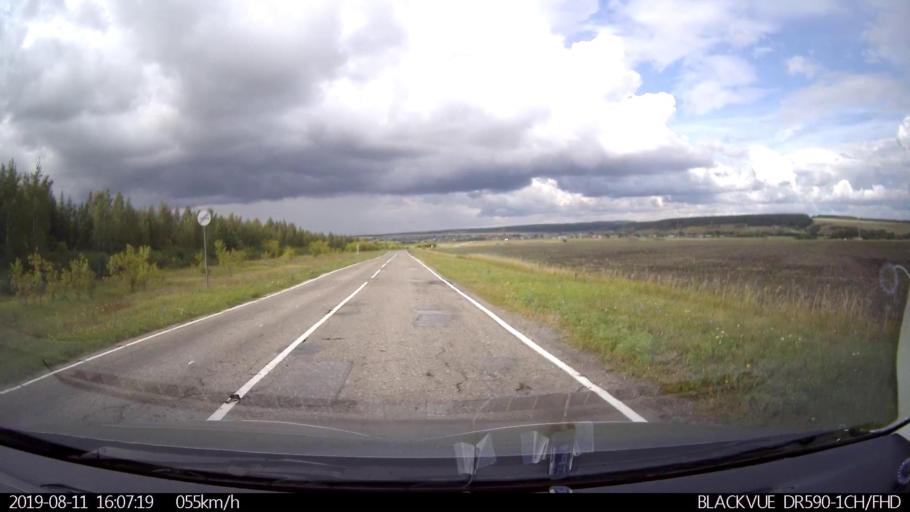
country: RU
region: Ulyanovsk
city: Ignatovka
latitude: 53.9756
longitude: 47.6478
